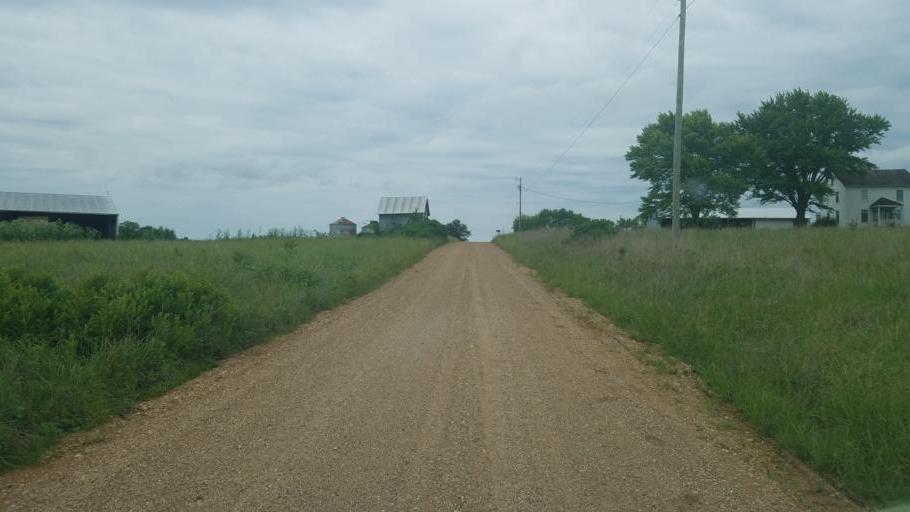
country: US
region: Missouri
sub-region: Moniteau County
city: Tipton
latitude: 38.5273
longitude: -92.7442
